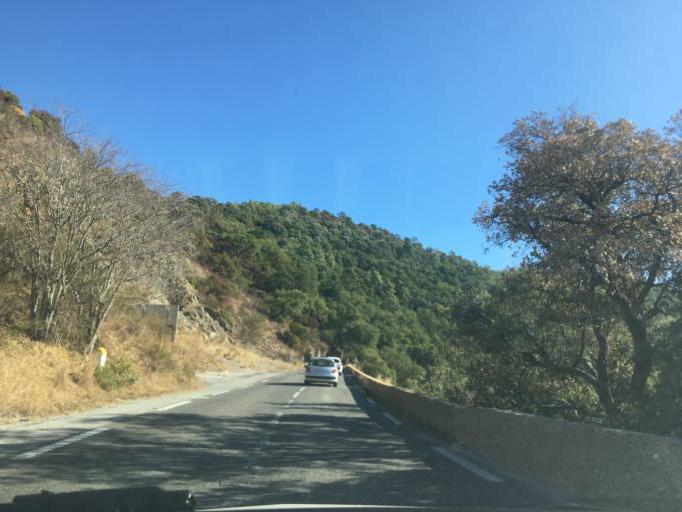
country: FR
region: Provence-Alpes-Cote d'Azur
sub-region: Departement du Var
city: La Garde-Freinet
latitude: 43.3313
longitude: 6.4541
